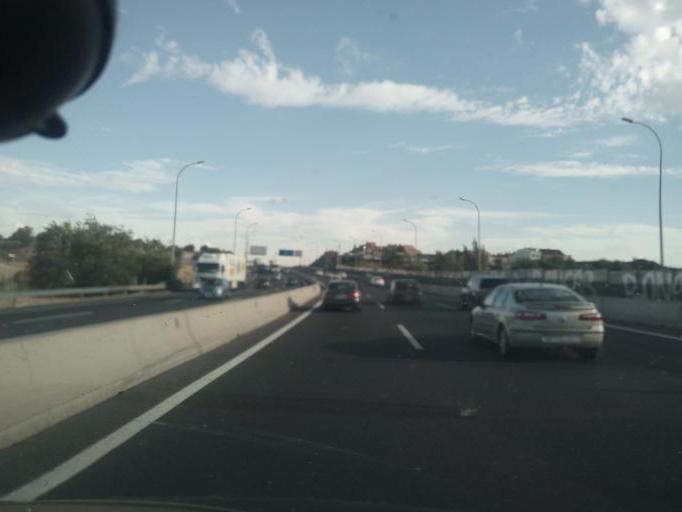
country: ES
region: Madrid
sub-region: Provincia de Madrid
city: Valdemoro
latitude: 40.1879
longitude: -3.6723
